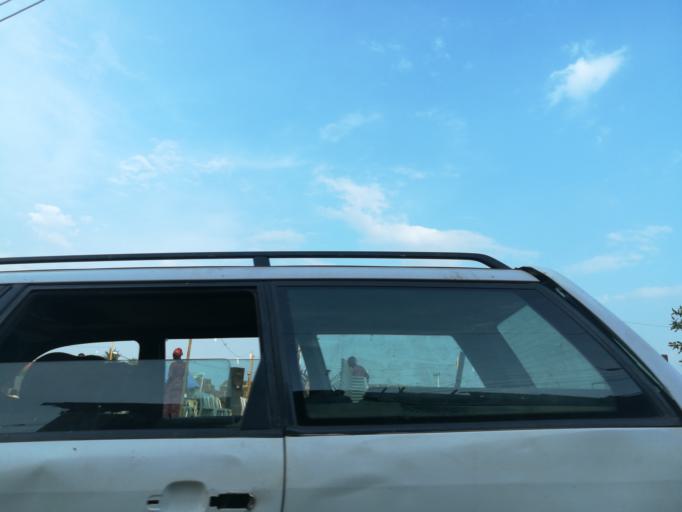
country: NG
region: Lagos
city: Ojota
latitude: 6.5966
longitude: 3.3963
